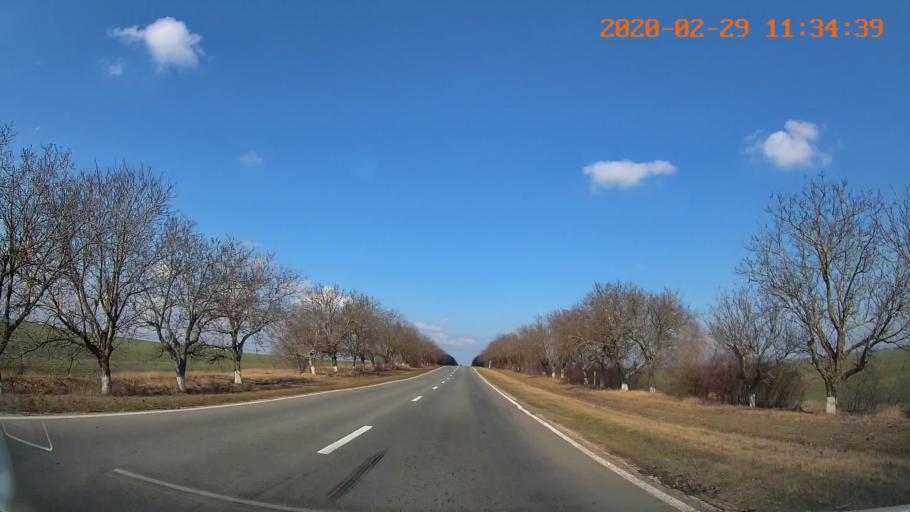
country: MD
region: Rezina
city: Saharna
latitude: 47.5689
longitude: 29.0714
